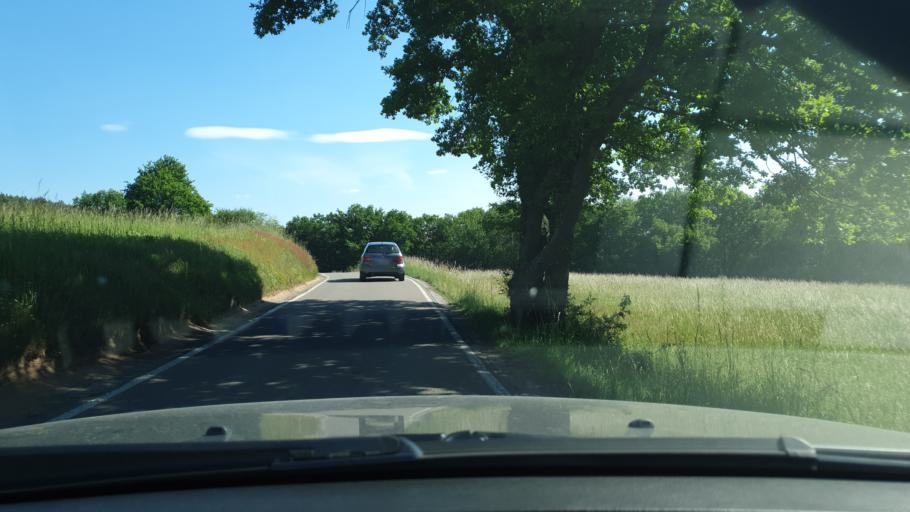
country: DE
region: Rheinland-Pfalz
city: Otterberg
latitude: 49.4852
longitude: 7.7698
